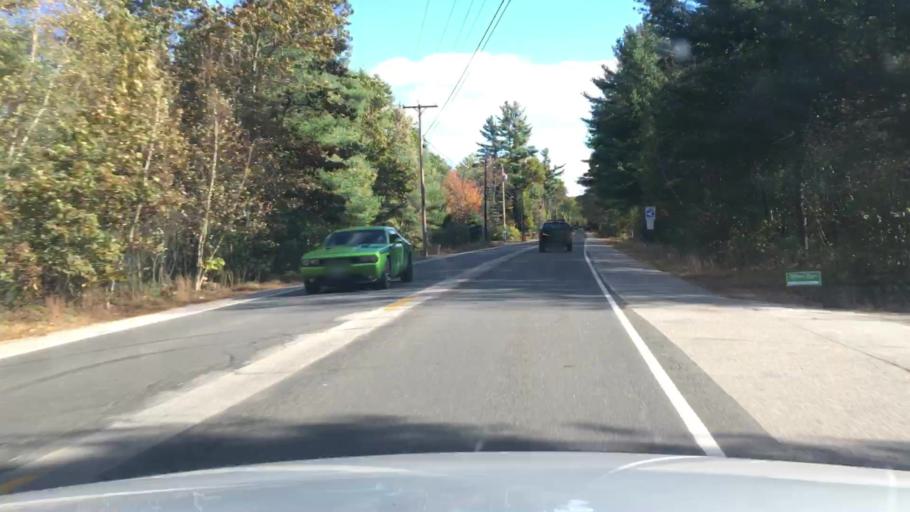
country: US
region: Maine
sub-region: York County
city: South Sanford
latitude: 43.3773
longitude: -70.6813
